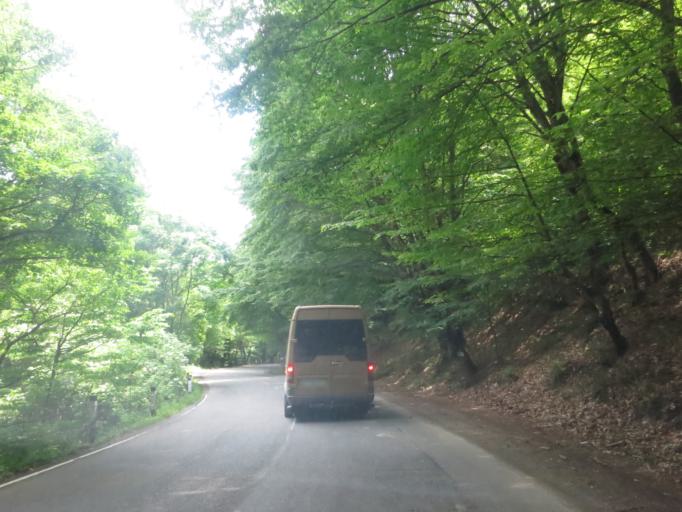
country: GE
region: Kakheti
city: Sagarejo
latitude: 41.8641
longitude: 45.3290
